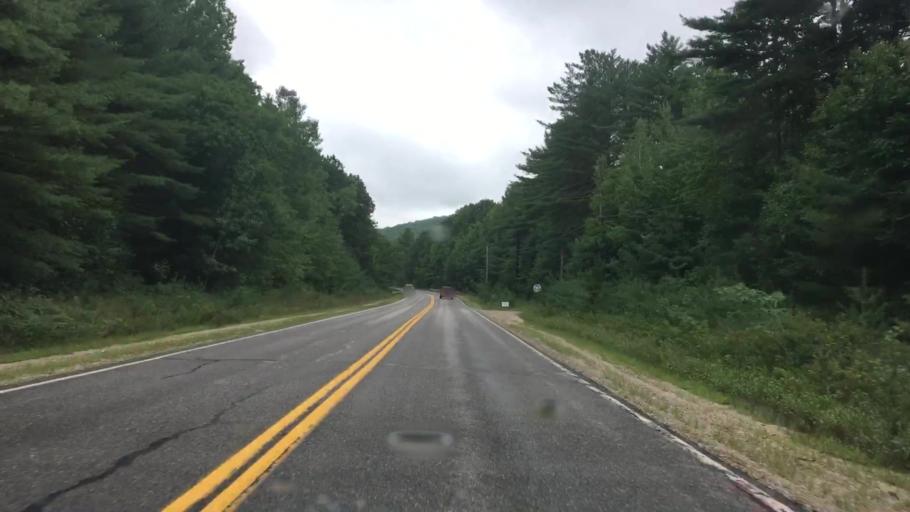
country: US
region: Maine
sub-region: Oxford County
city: Brownfield
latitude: 43.9778
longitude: -70.9262
